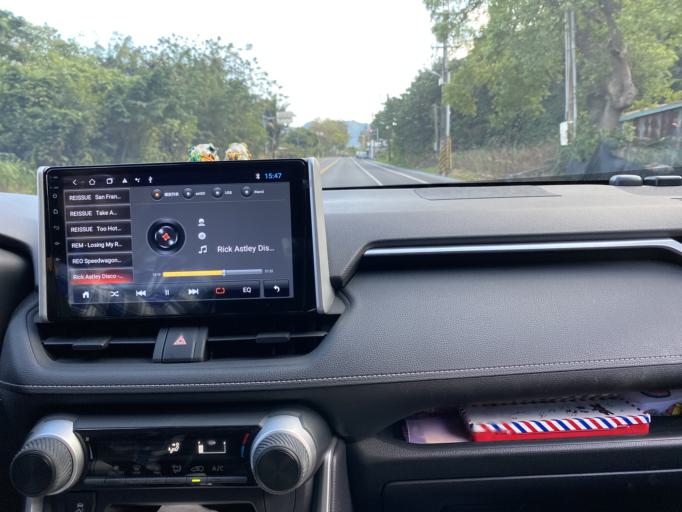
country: TW
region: Taiwan
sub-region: Taitung
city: Taitung
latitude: 22.9065
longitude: 121.1366
